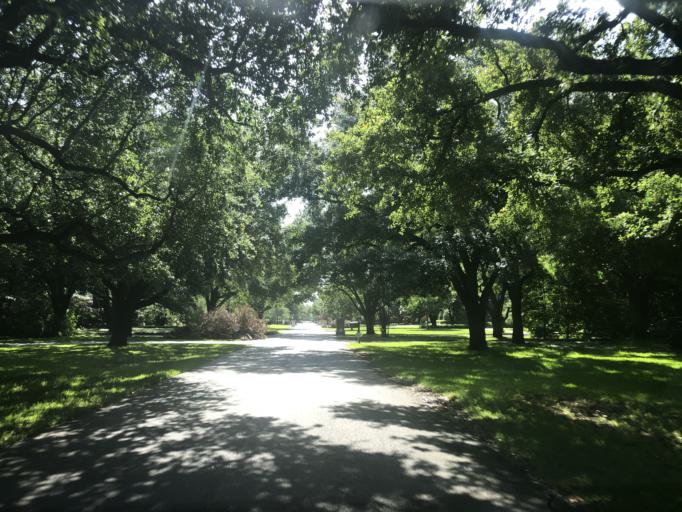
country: US
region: Texas
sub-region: Dallas County
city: University Park
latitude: 32.8911
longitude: -96.8145
